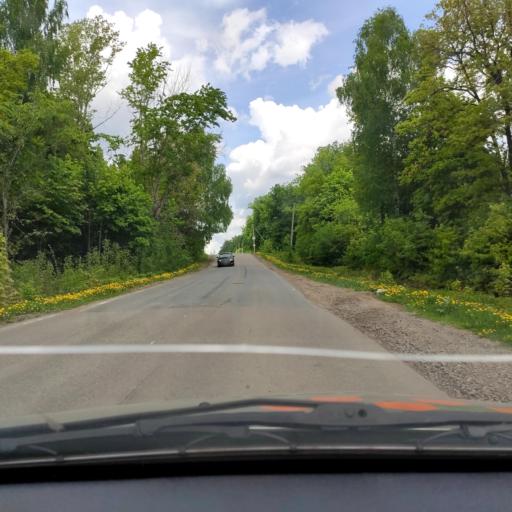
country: RU
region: Bashkortostan
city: Avdon
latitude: 54.6508
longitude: 55.7025
